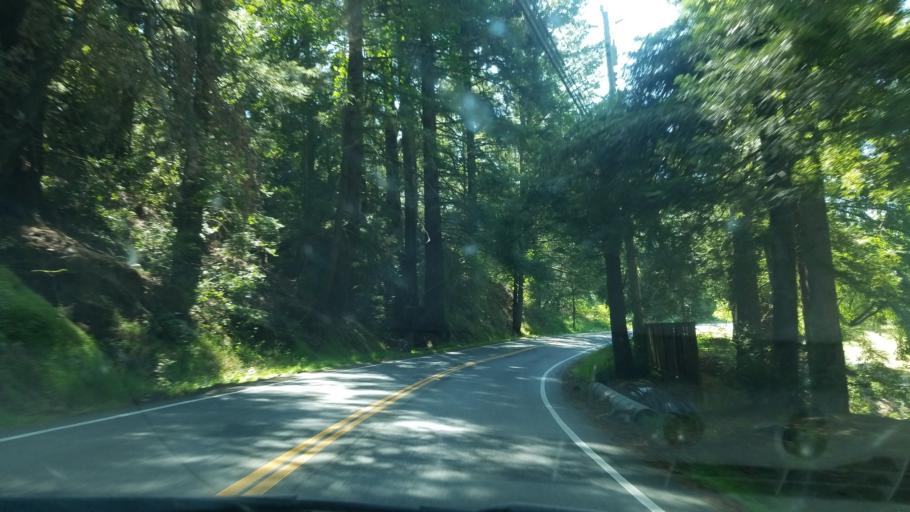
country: US
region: California
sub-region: Santa Clara County
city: Lexington Hills
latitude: 37.1124
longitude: -121.9436
